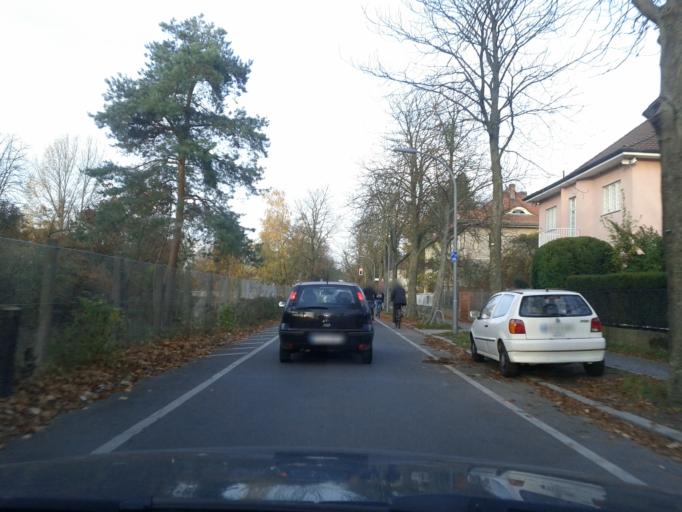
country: DE
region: Berlin
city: Dahlem
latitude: 52.4560
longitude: 13.2887
